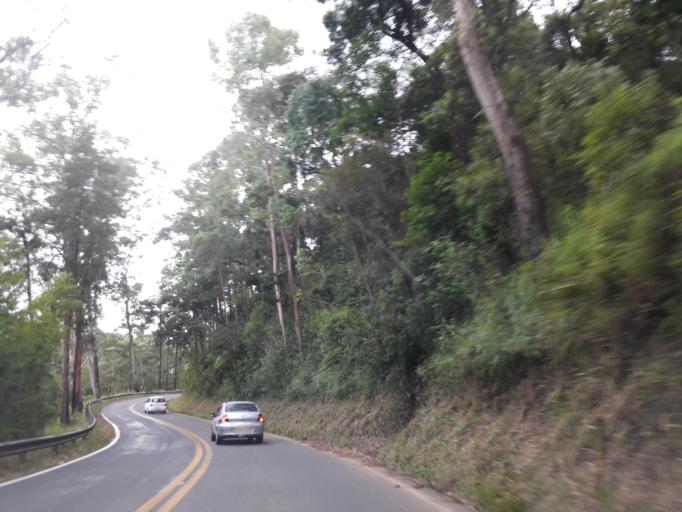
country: BR
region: Sao Paulo
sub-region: Aruja
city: Aruja
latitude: -23.3448
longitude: -46.4280
